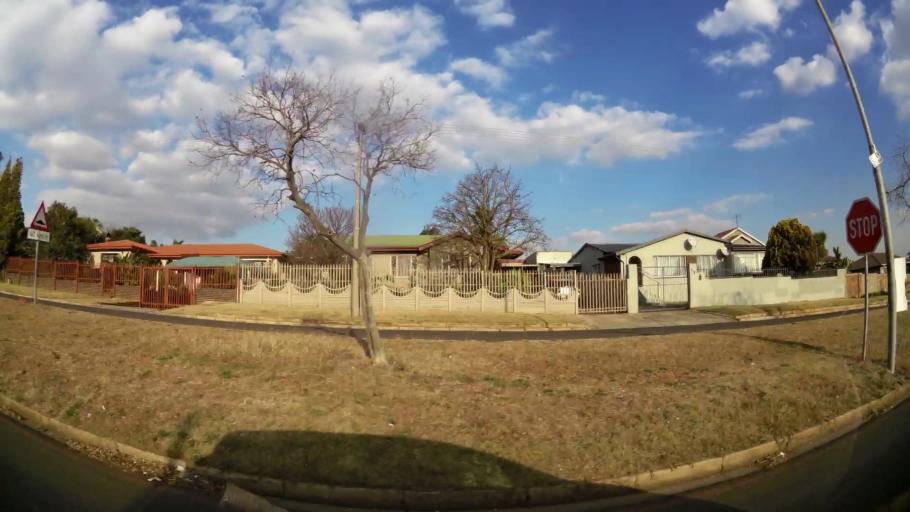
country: ZA
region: Gauteng
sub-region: West Rand District Municipality
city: Krugersdorp
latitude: -26.0924
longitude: 27.7550
